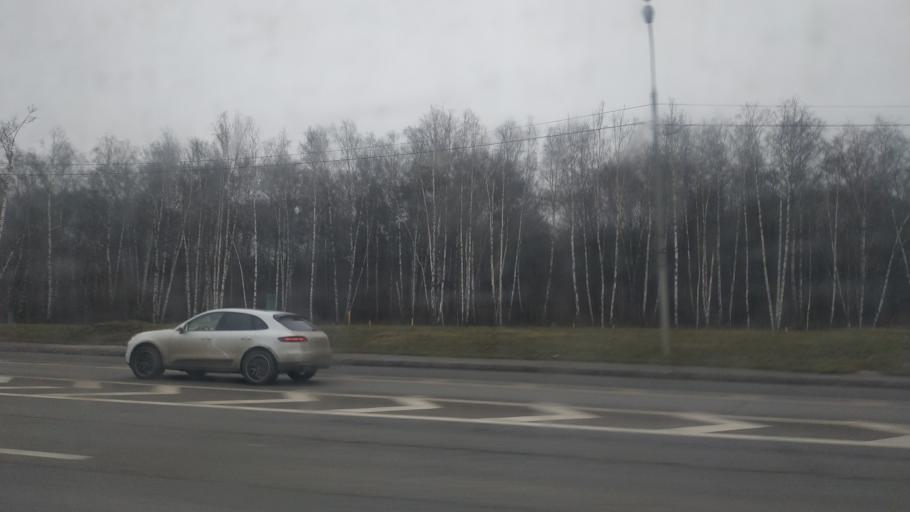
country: RU
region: Moscow
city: Severnyy
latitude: 55.9274
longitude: 37.5471
